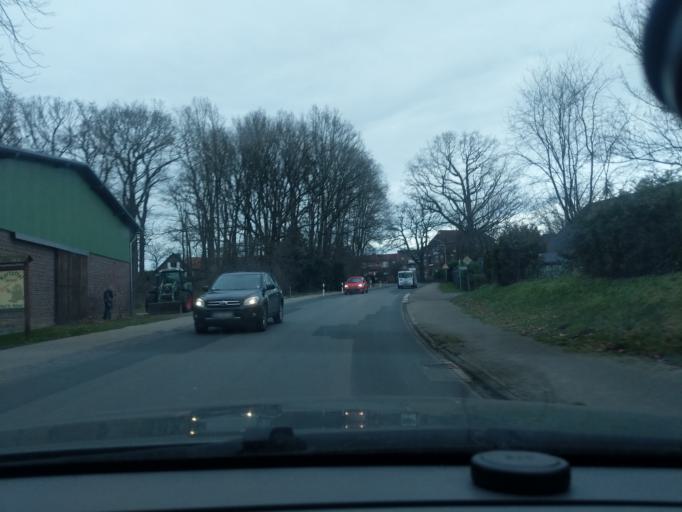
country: DE
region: Lower Saxony
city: Beckdorf
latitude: 53.4107
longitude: 9.6103
